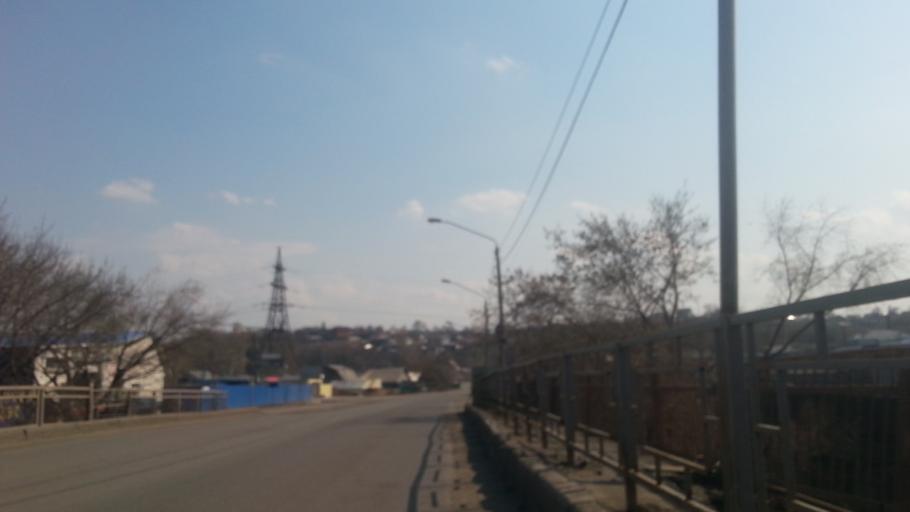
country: RU
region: Altai Krai
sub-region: Gorod Barnaulskiy
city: Barnaul
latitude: 53.3226
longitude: 83.7680
